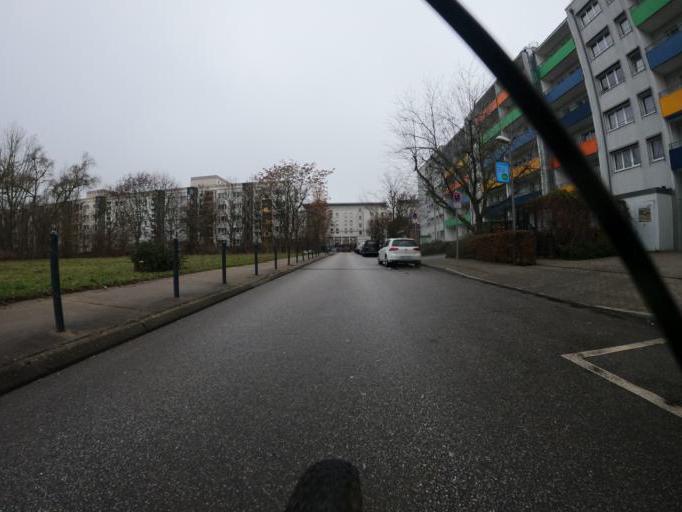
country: DE
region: Berlin
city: Marzahn
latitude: 52.5547
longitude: 13.5606
